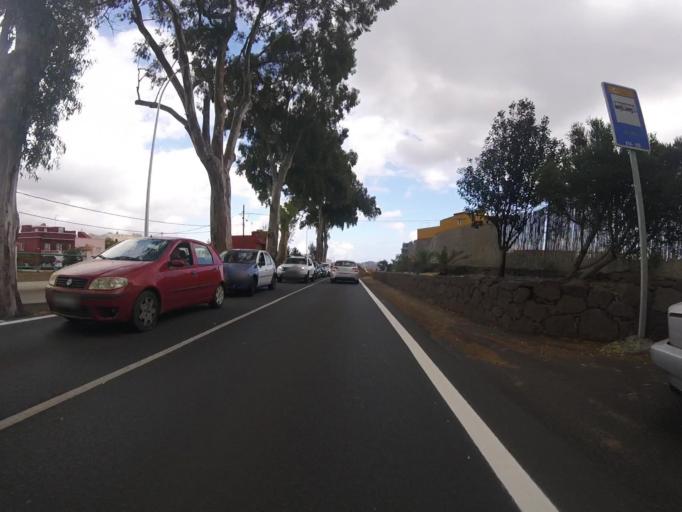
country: ES
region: Canary Islands
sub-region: Provincia de Las Palmas
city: Vega de San Mateo
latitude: 28.0148
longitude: -15.5264
